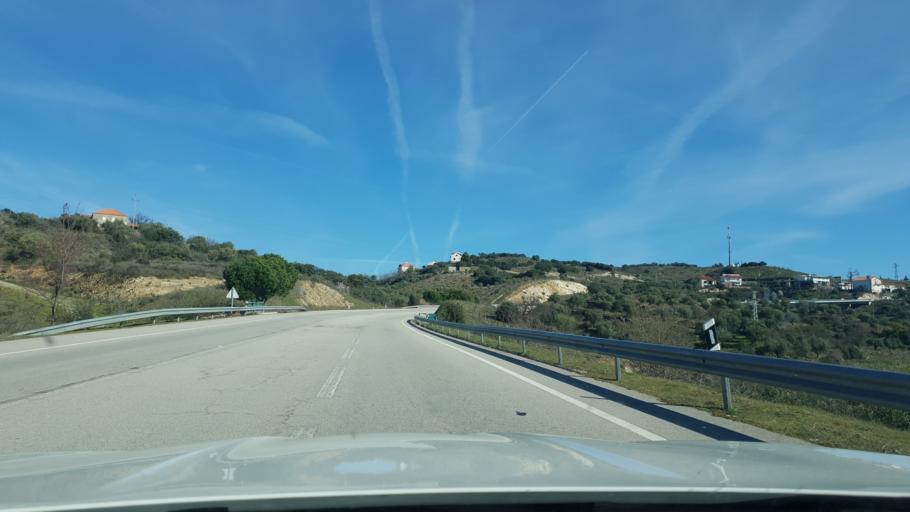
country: PT
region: Braganca
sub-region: Torre de Moncorvo
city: Torre de Moncorvo
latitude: 41.1783
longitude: -7.0625
